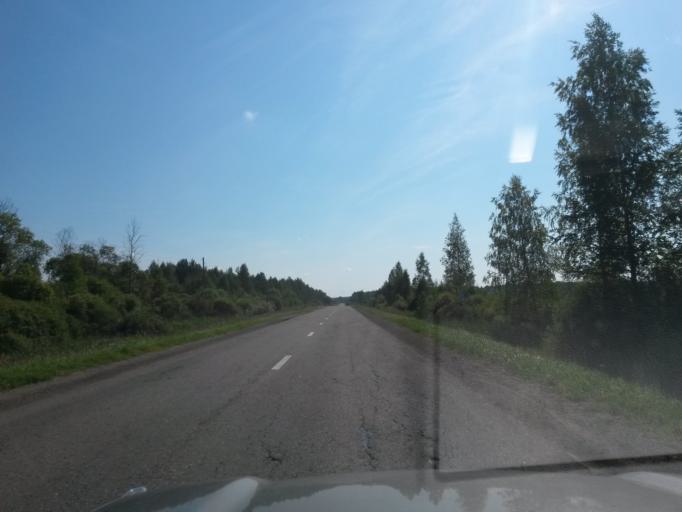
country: RU
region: Jaroslavl
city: Gavrilov-Yam
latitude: 57.3082
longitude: 39.9649
